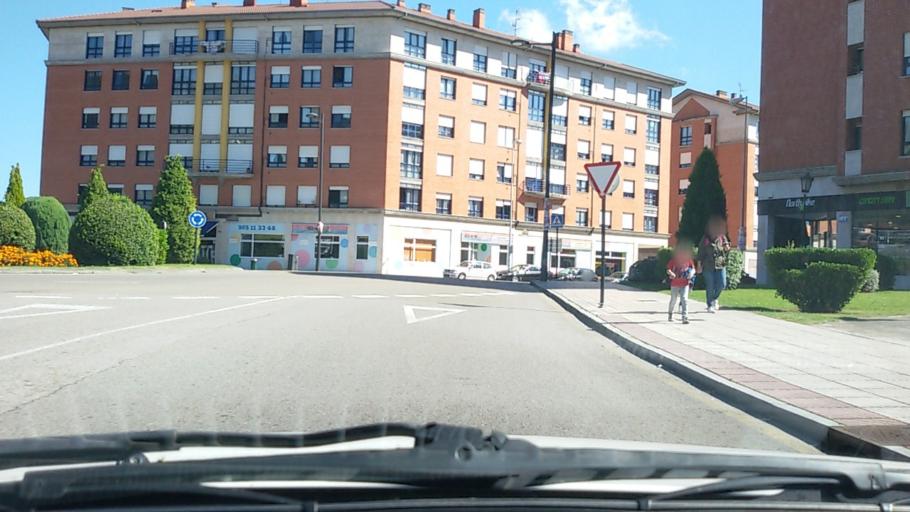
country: ES
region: Asturias
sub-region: Province of Asturias
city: Oviedo
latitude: 43.3779
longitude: -5.8326
